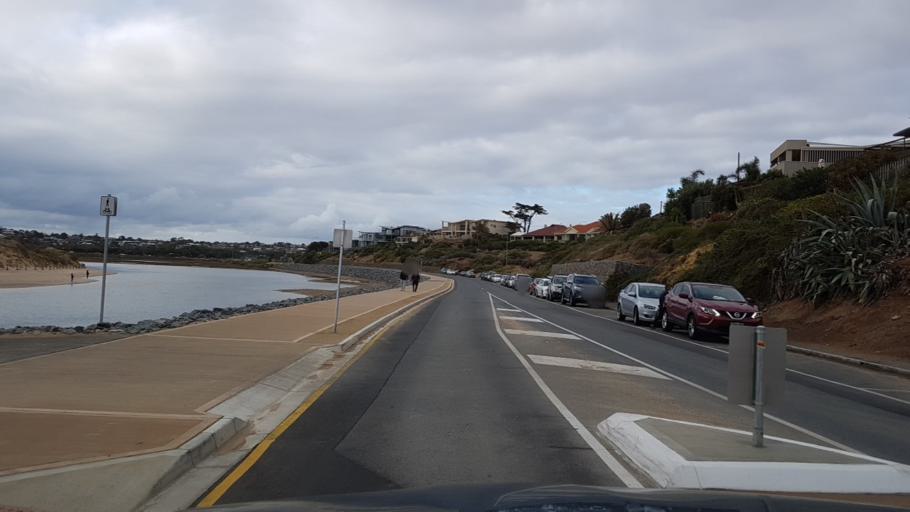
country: AU
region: South Australia
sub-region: Adelaide
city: Port Noarlunga
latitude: -35.1601
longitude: 138.4727
